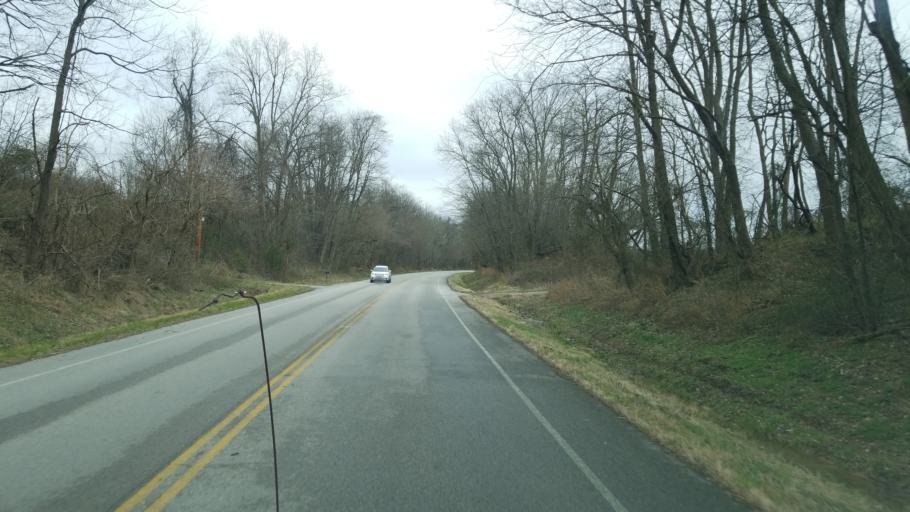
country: US
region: Kentucky
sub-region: Bracken County
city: Augusta
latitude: 38.7890
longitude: -83.9421
